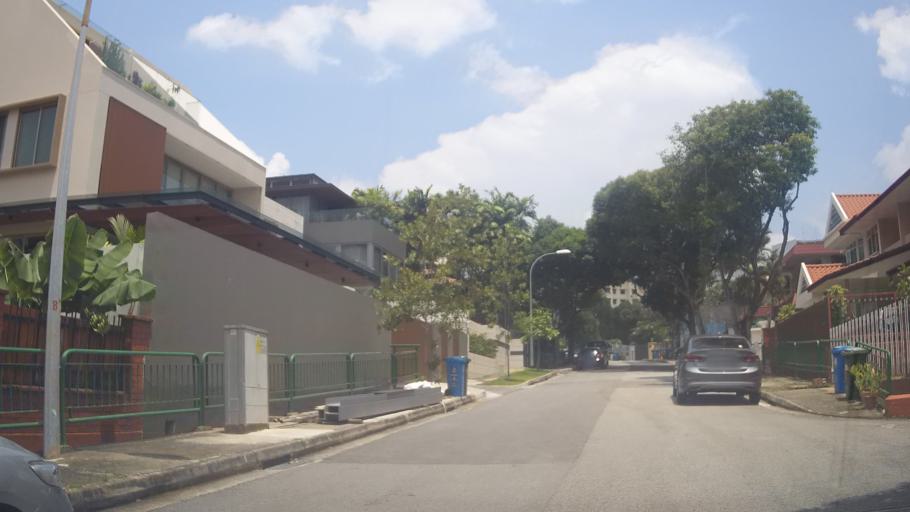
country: SG
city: Singapore
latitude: 1.3590
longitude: 103.8694
